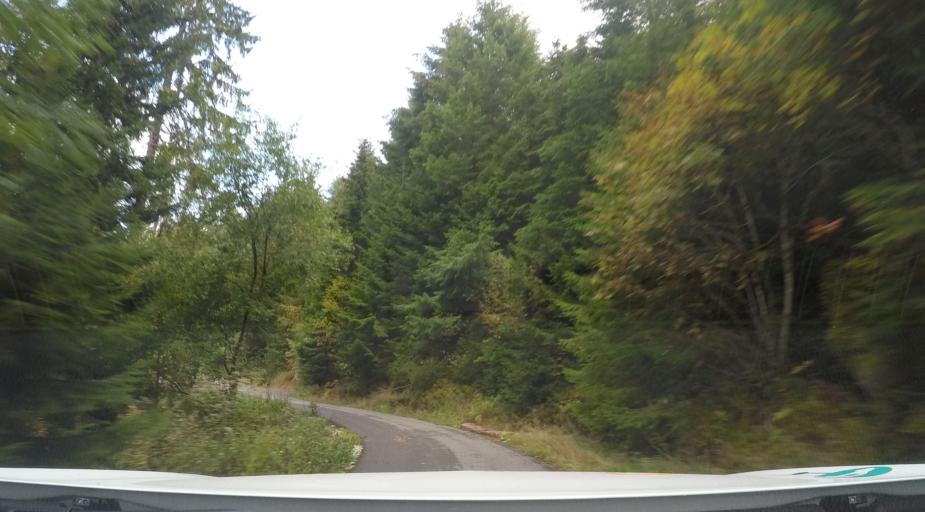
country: DE
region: Baden-Wuerttemberg
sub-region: Karlsruhe Region
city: Baiersbronn
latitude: 48.5617
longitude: 8.3444
